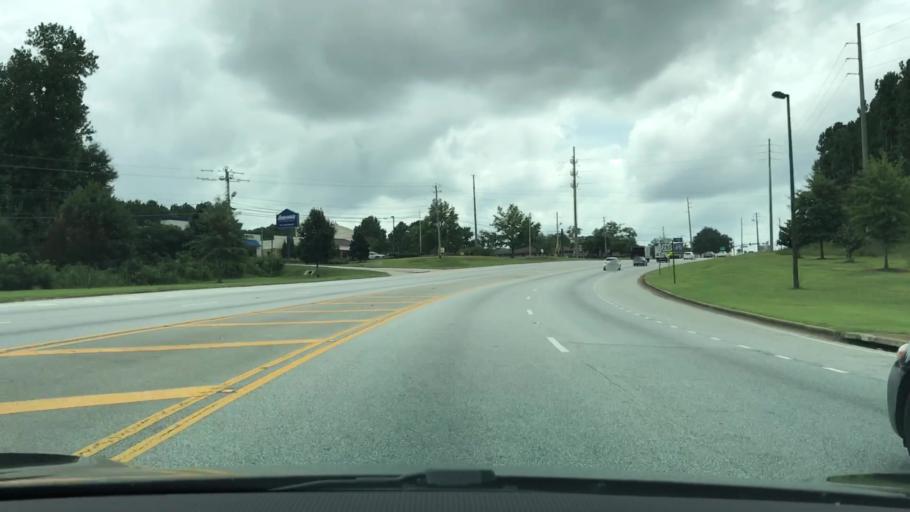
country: US
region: Alabama
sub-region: Lee County
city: Opelika
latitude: 32.6292
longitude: -85.4056
